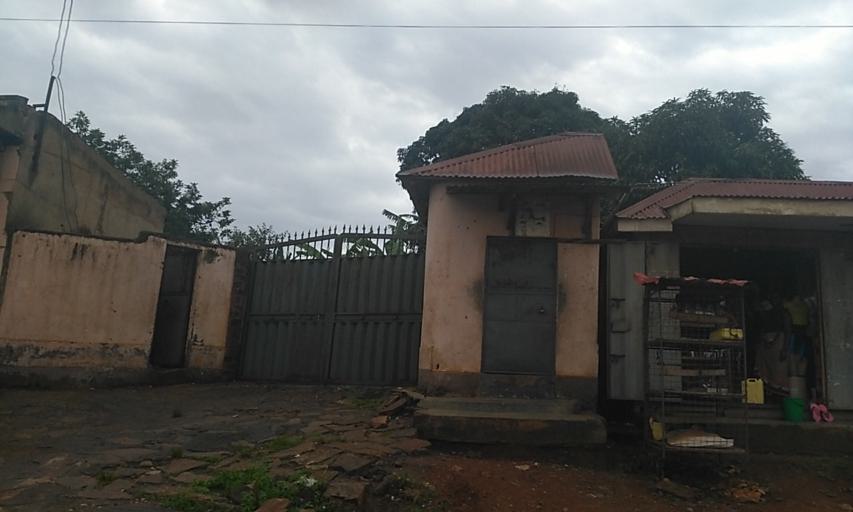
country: UG
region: Central Region
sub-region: Wakiso District
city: Bweyogerere
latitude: 0.3555
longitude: 32.6649
